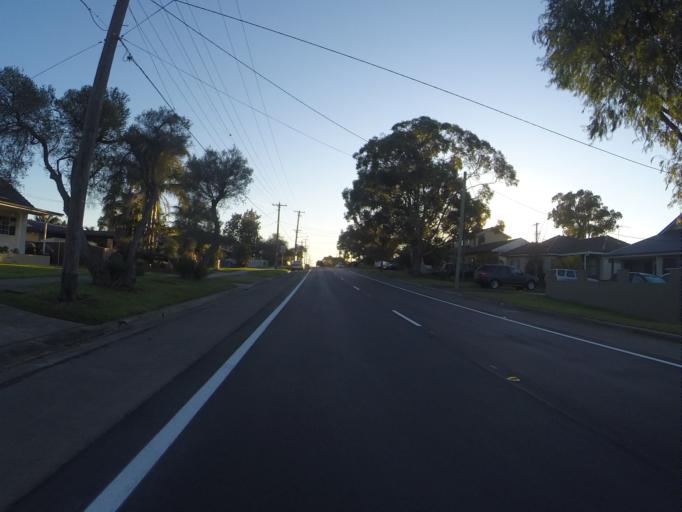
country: AU
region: New South Wales
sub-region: Sutherland Shire
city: Engadine
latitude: -34.0552
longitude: 151.0057
